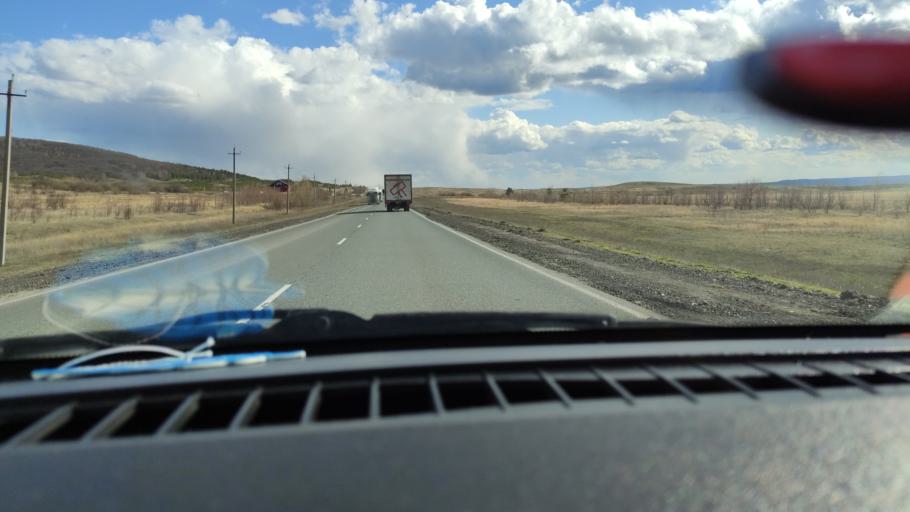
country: RU
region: Saratov
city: Alekseyevka
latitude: 52.3079
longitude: 47.9253
